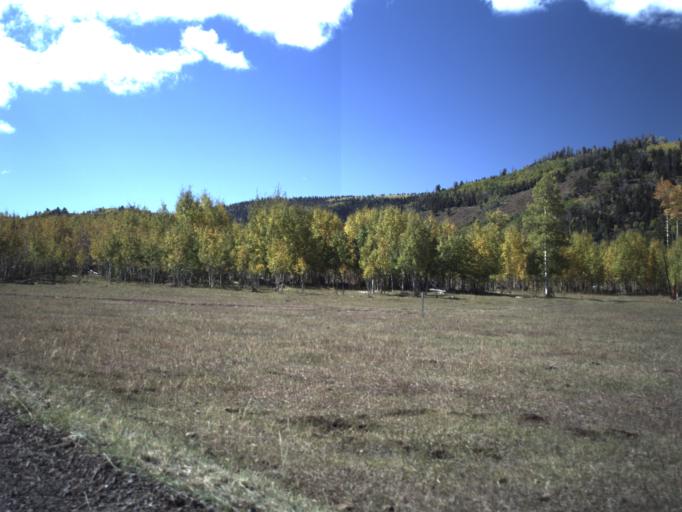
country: US
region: Utah
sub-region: Piute County
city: Junction
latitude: 38.2492
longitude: -112.3395
